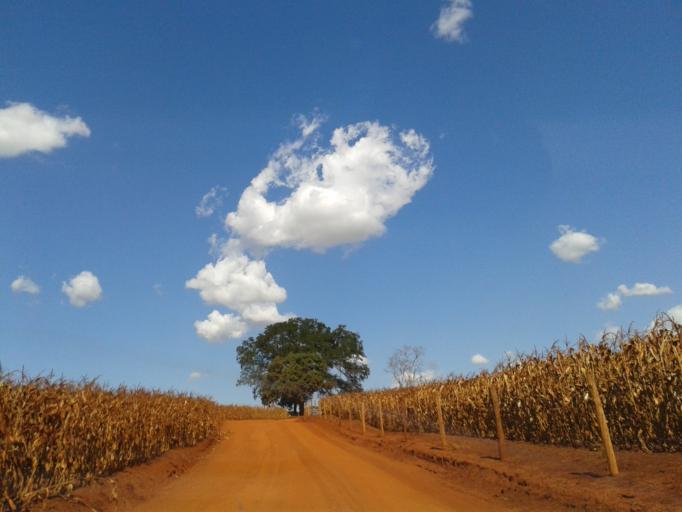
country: BR
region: Minas Gerais
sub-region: Capinopolis
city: Capinopolis
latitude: -18.6132
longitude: -49.4949
